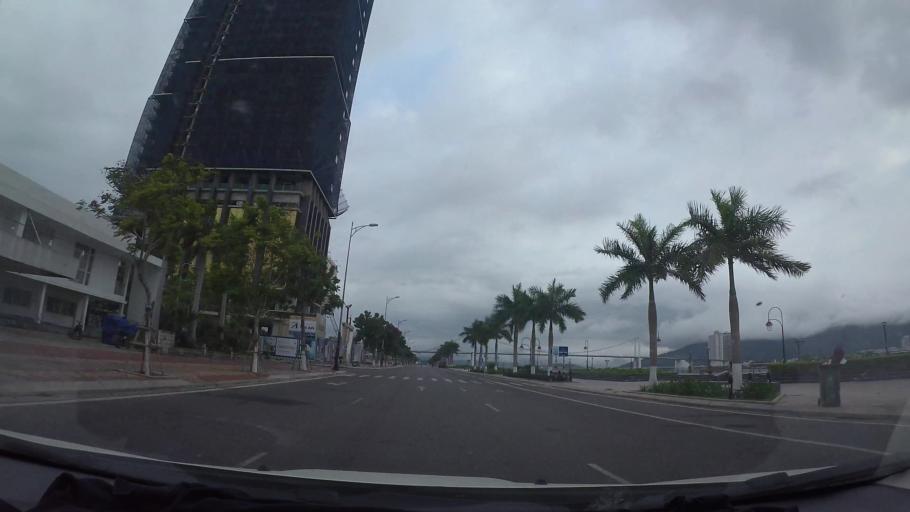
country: VN
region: Da Nang
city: Da Nang
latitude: 16.0864
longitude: 108.2217
